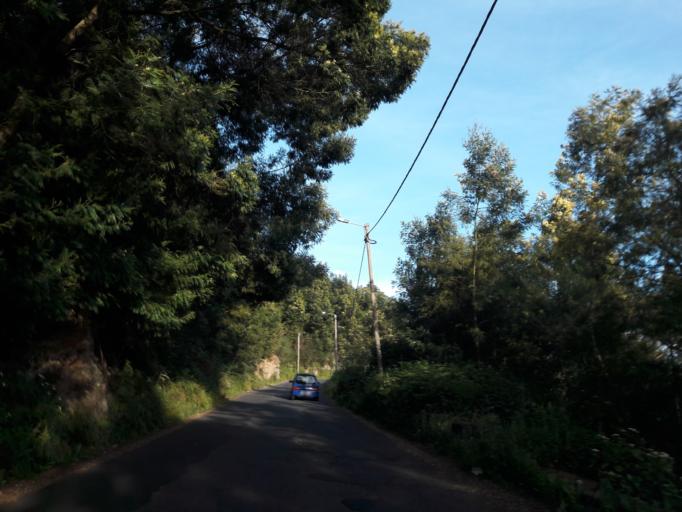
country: PT
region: Madeira
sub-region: Santa Cruz
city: Camacha
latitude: 32.6671
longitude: -16.8437
